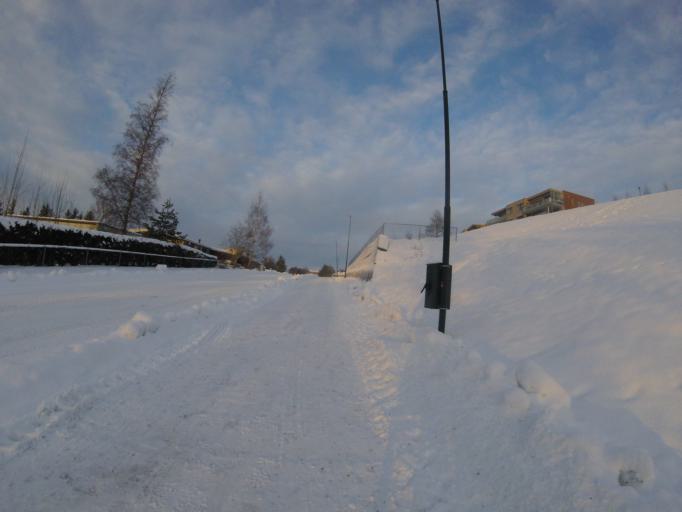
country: NO
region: Akershus
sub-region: Skedsmo
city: Lillestrom
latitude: 59.9690
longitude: 11.0547
